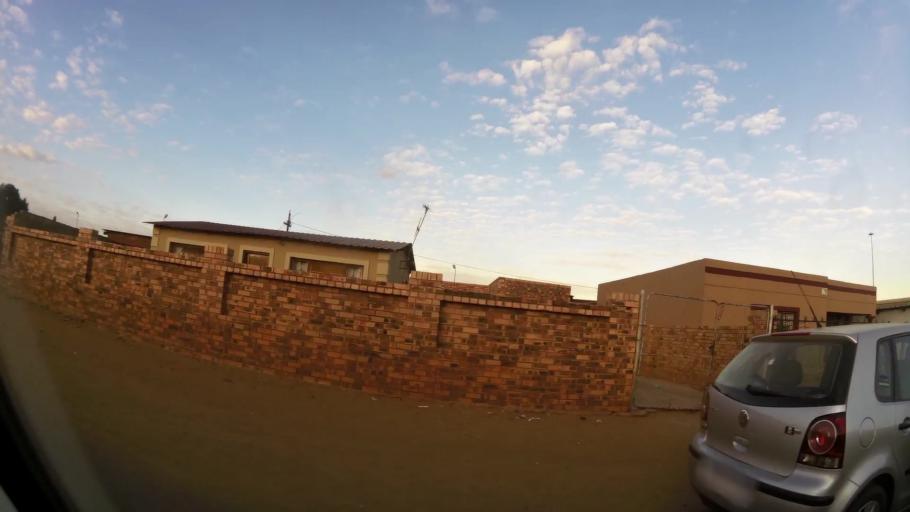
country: ZA
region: Gauteng
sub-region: City of Tshwane Metropolitan Municipality
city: Pretoria
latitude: -25.7156
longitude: 28.3550
